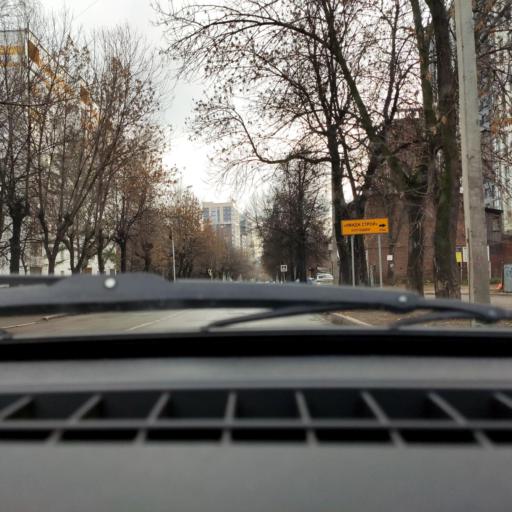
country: RU
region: Bashkortostan
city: Ufa
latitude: 54.7232
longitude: 55.9584
